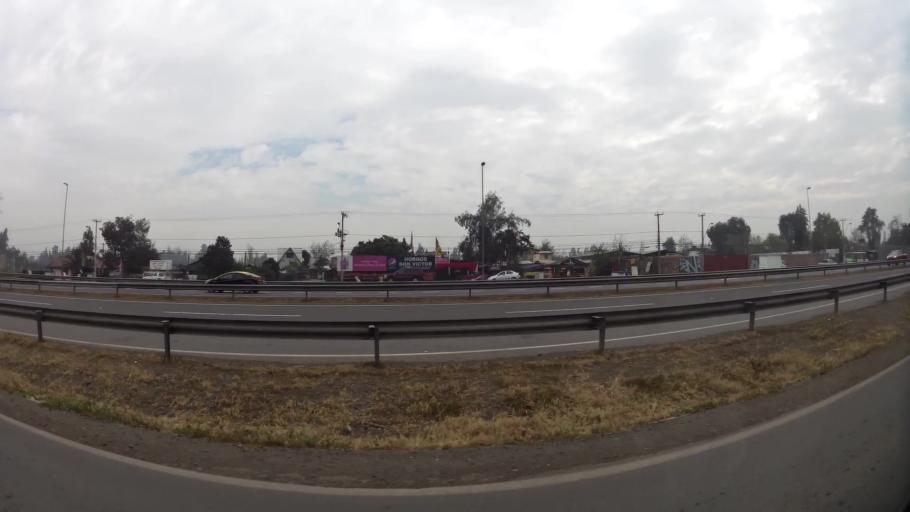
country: CL
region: Santiago Metropolitan
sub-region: Provincia de Chacabuco
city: Chicureo Abajo
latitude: -33.2360
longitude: -70.6950
